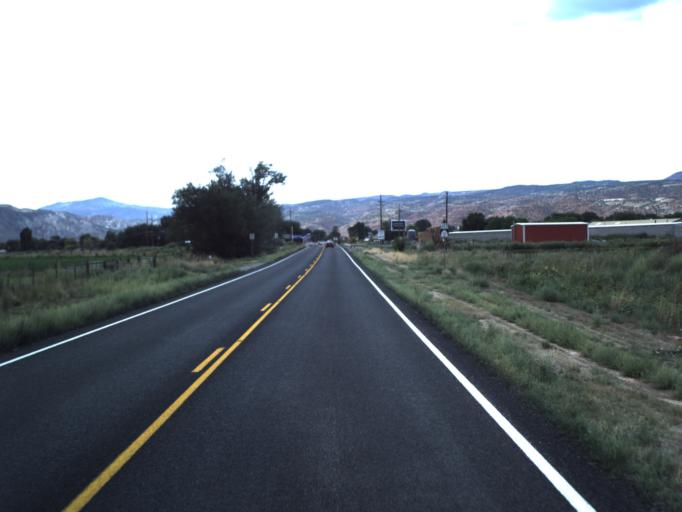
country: US
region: Utah
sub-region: Sevier County
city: Richfield
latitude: 38.7726
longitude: -112.0646
